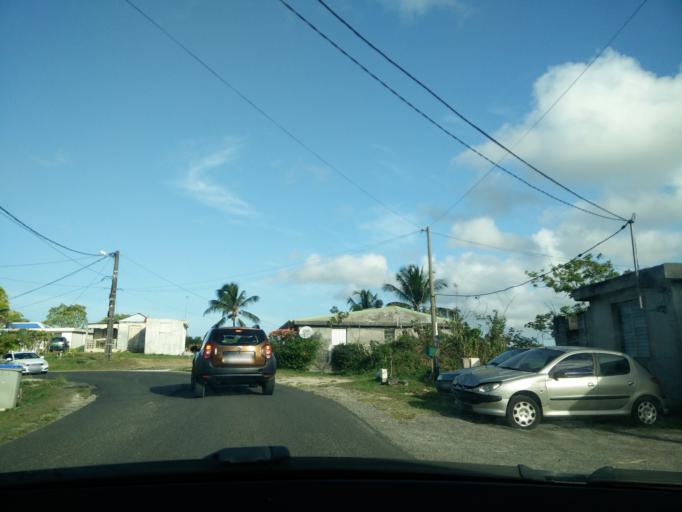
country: GP
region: Guadeloupe
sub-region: Guadeloupe
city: Sainte-Anne
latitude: 16.2793
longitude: -61.4122
